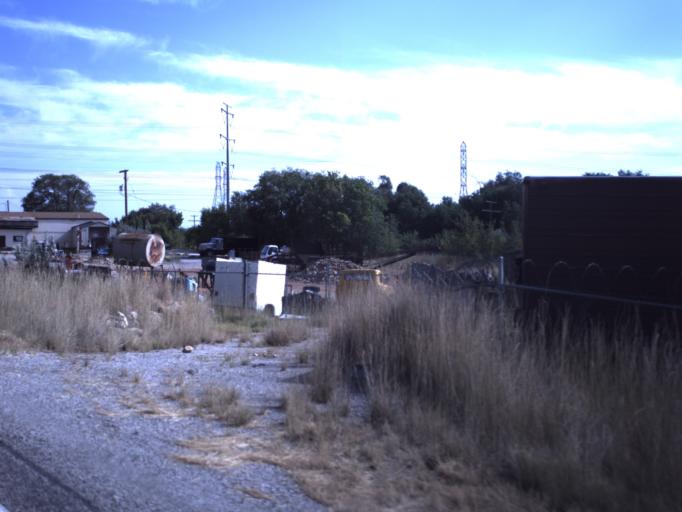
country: US
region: Utah
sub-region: Box Elder County
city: South Willard
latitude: 41.3405
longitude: -112.0314
